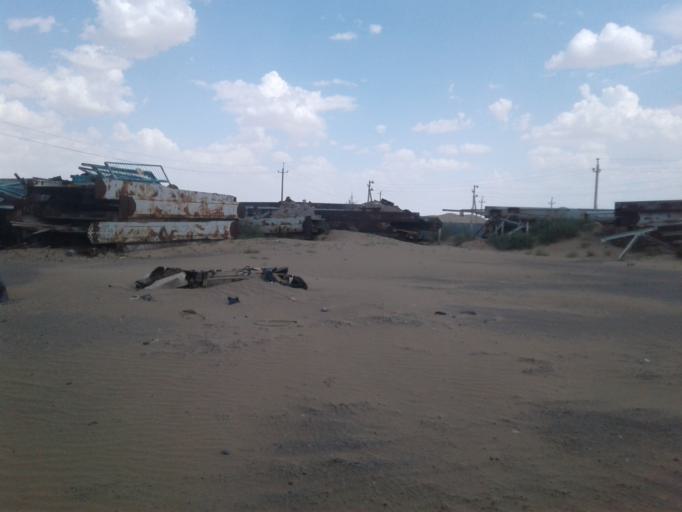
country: TM
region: Ahal
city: Abadan
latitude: 38.7538
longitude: 58.4878
